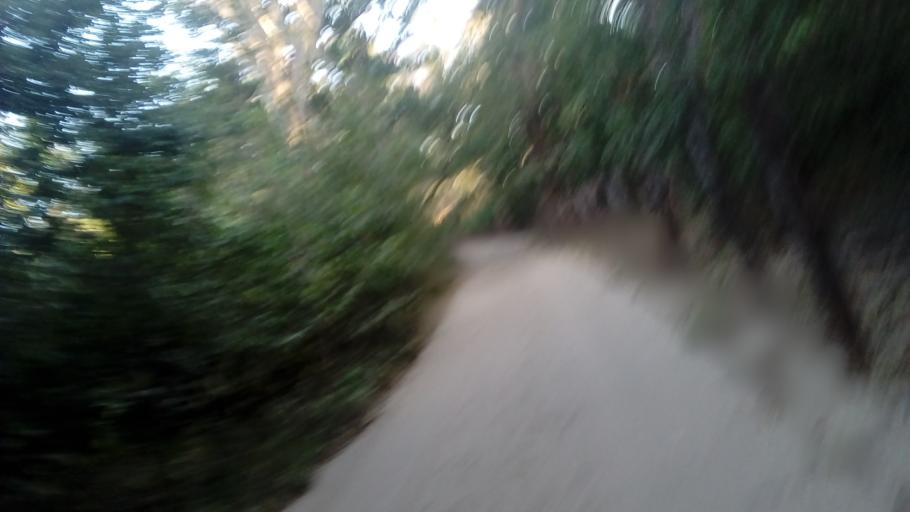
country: CR
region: Guanacaste
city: Sardinal
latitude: 10.3997
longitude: -85.8174
